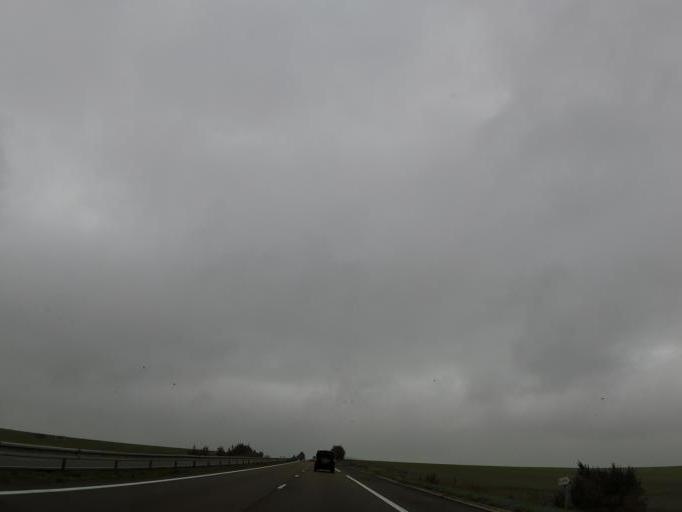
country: FR
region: Champagne-Ardenne
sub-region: Departement de la Marne
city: Mourmelon-le-Grand
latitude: 49.0795
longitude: 4.2629
